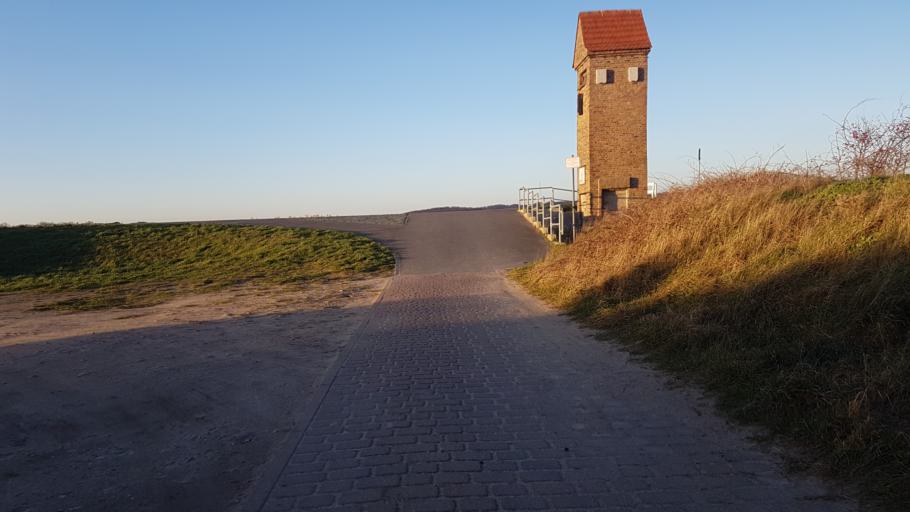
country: DE
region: Mecklenburg-Vorpommern
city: Ostseebad Sellin
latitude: 54.3576
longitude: 13.6963
